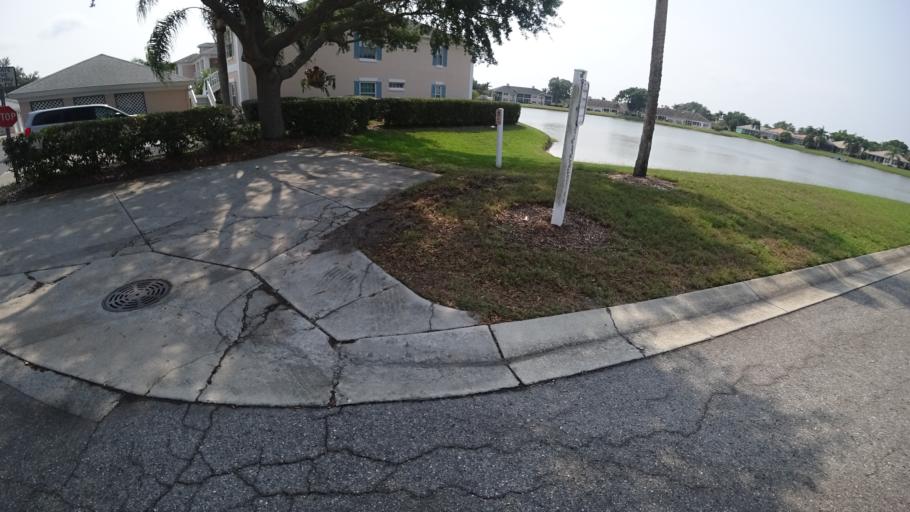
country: US
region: Florida
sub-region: Manatee County
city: Samoset
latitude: 27.4575
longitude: -82.5111
